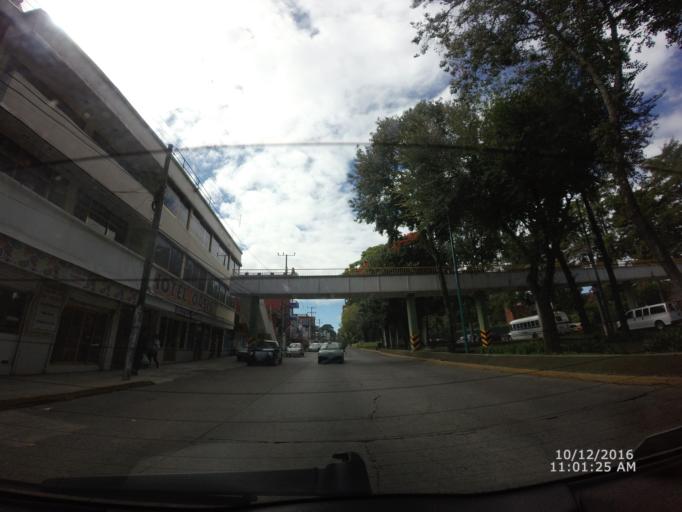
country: TR
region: Sivas
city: Karayun
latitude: 39.6721
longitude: 37.2369
